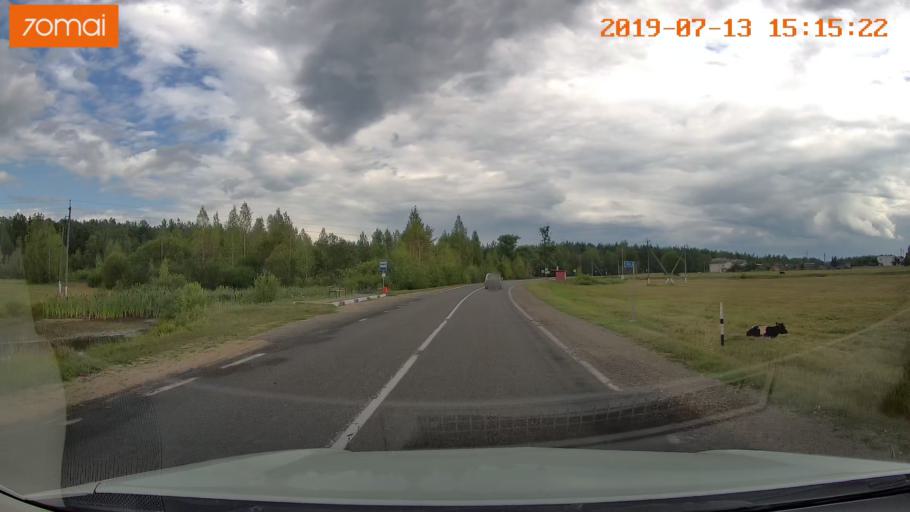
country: BY
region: Mogilev
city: Hlusha
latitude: 53.1177
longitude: 28.8263
